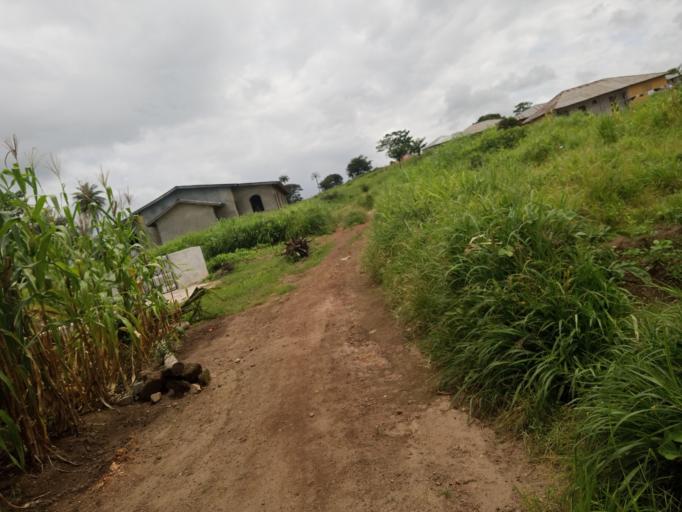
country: SL
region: Northern Province
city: Kamakwie
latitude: 9.5033
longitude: -12.2540
